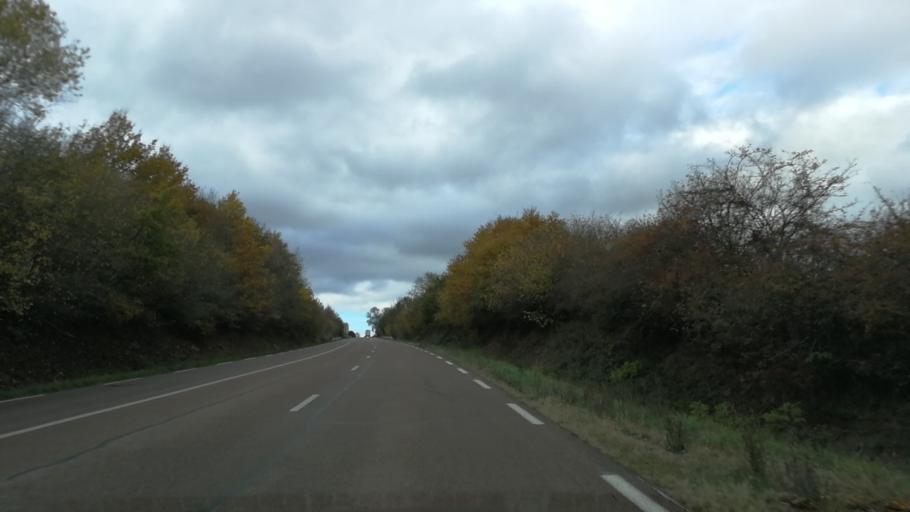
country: FR
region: Bourgogne
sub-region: Departement de la Cote-d'Or
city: Saulieu
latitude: 47.2606
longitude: 4.2656
